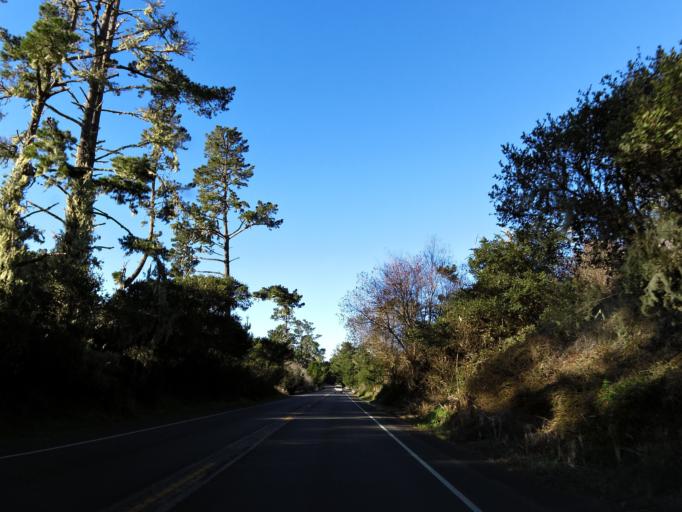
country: US
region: California
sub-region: Santa Cruz County
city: Bonny Doon
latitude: 37.1185
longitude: -122.3046
